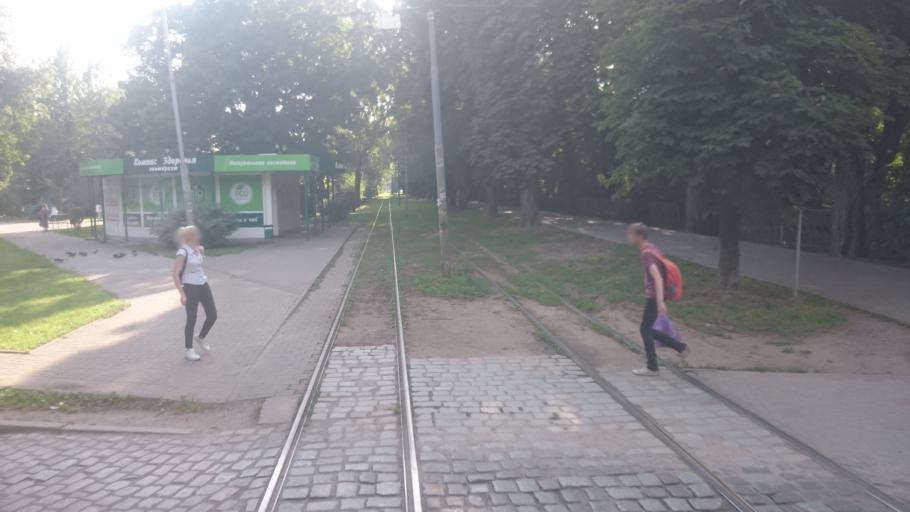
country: RU
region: Kaliningrad
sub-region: Gorod Kaliningrad
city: Kaliningrad
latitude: 54.7270
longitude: 20.4742
